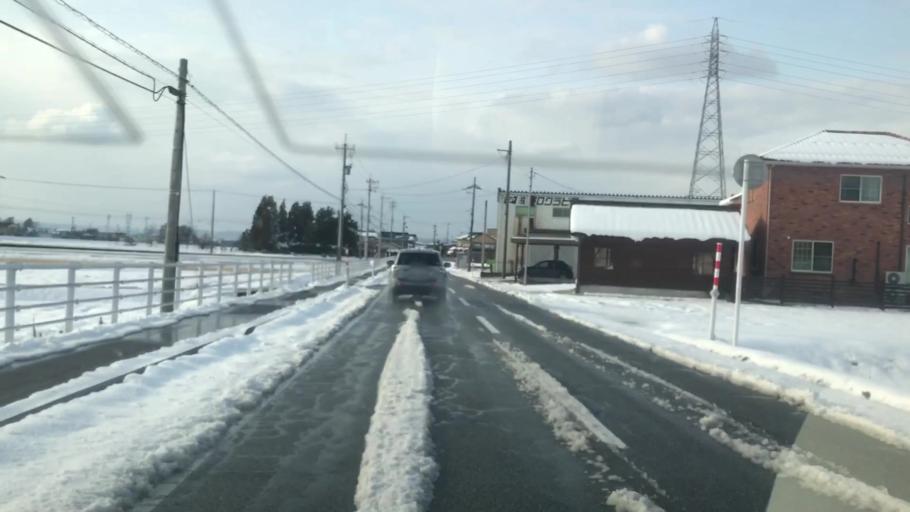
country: JP
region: Toyama
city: Toyama-shi
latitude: 36.6422
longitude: 137.2567
